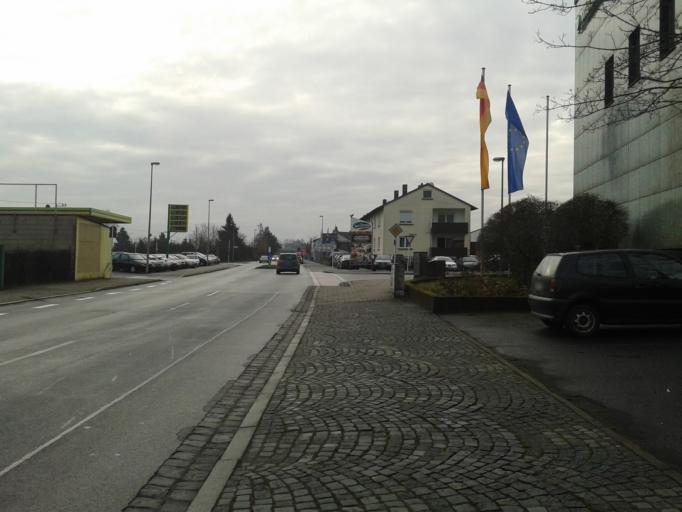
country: DE
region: Bavaria
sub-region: Upper Franconia
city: Hallstadt
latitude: 49.9130
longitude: 10.8826
